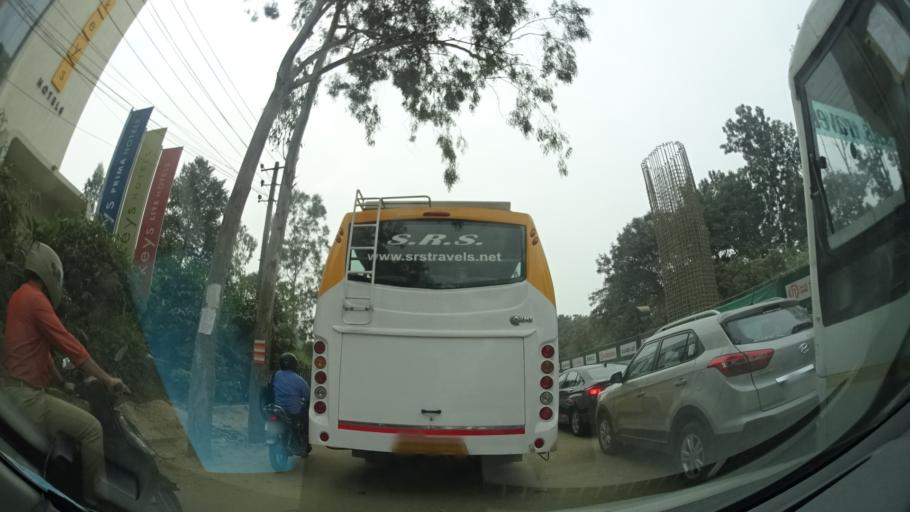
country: IN
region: Karnataka
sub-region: Bangalore Urban
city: Bangalore
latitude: 12.9793
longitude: 77.7093
